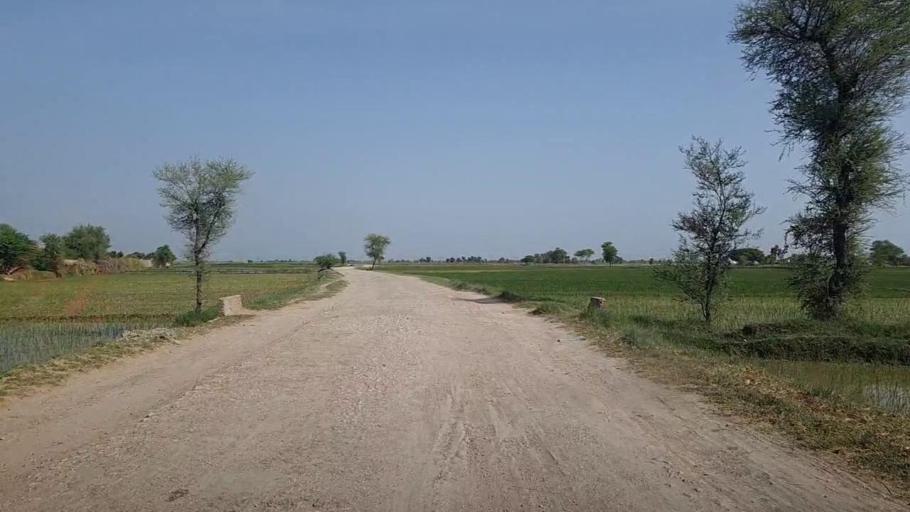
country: PK
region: Sindh
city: Mehar
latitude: 27.1151
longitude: 67.8437
